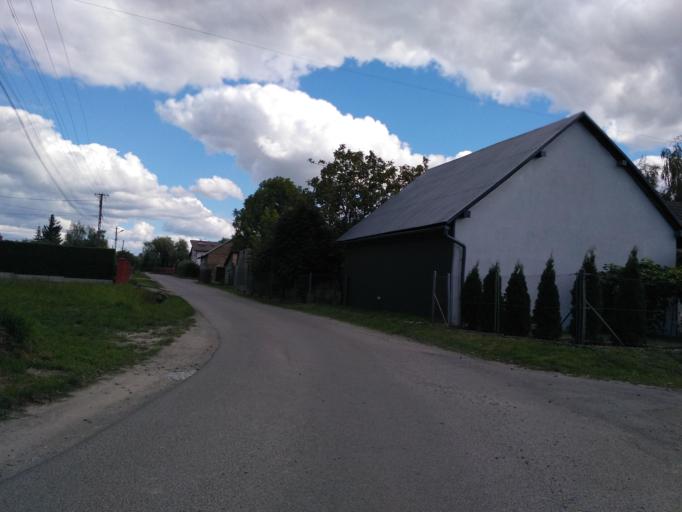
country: PL
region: Subcarpathian Voivodeship
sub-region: Powiat jasielski
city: Jaslo
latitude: 49.7627
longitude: 21.5202
